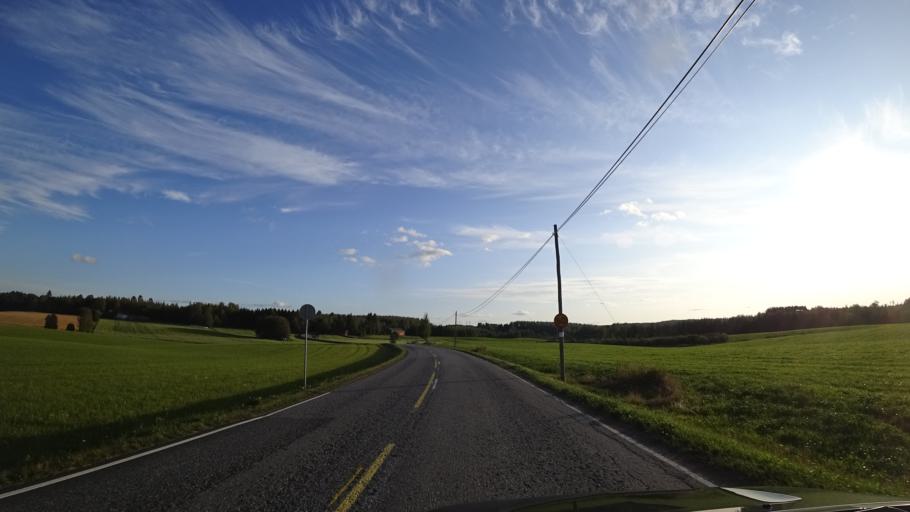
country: FI
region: Haeme
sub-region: Haemeenlinna
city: Lammi
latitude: 61.0427
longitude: 24.9359
